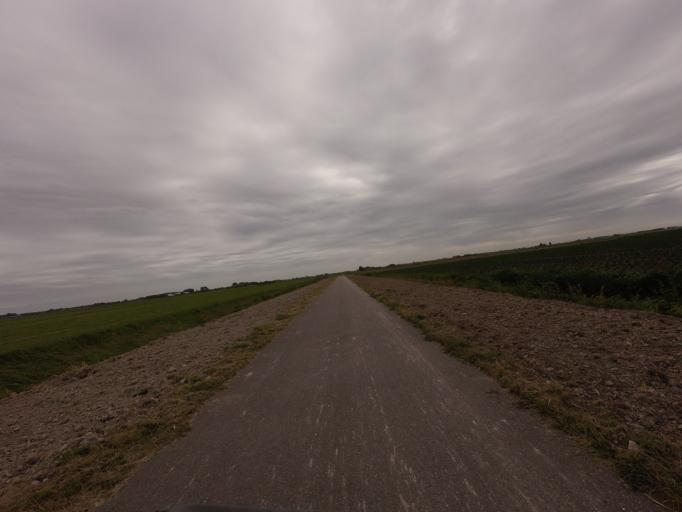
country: NL
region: North Holland
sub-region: Gemeente Medemblik
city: Opperdoes
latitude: 52.7378
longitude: 5.0585
